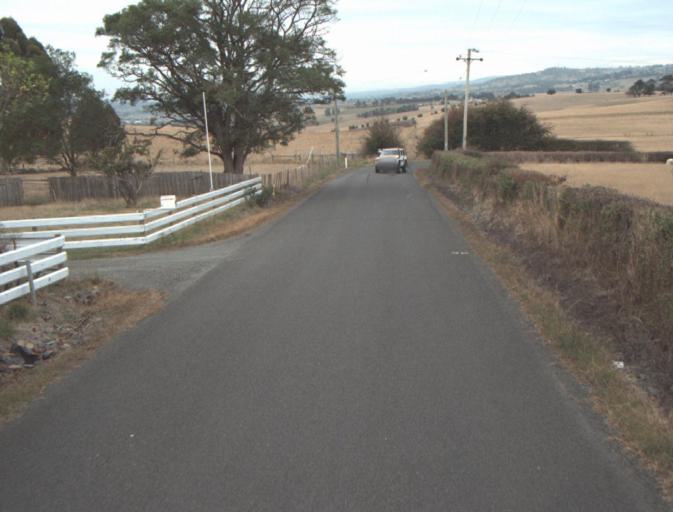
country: AU
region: Tasmania
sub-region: Northern Midlands
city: Evandale
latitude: -41.5098
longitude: 147.2497
